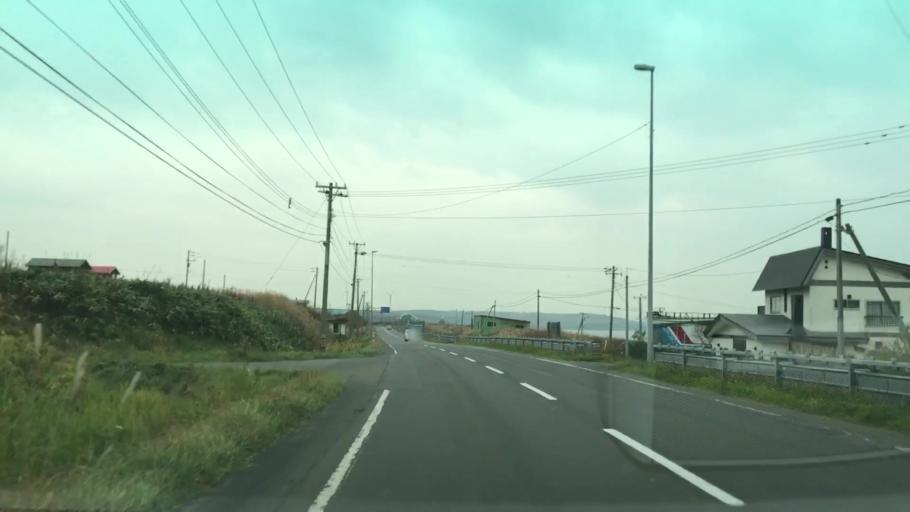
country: JP
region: Hokkaido
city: Ishikari
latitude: 43.3430
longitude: 141.4235
